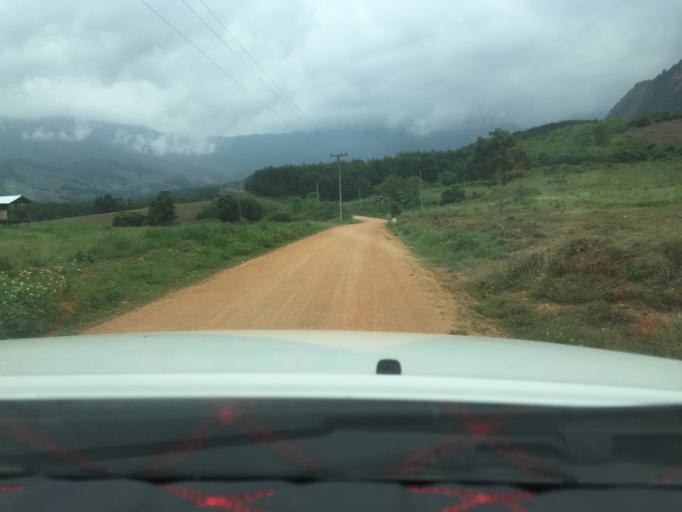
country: TH
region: Phayao
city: Phu Sang
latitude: 19.7401
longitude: 100.4640
